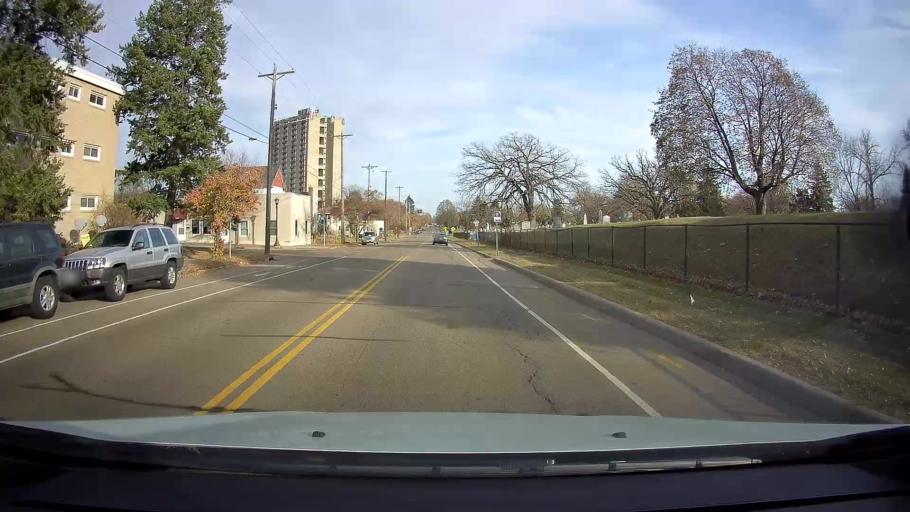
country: US
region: Minnesota
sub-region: Ramsey County
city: Falcon Heights
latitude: 44.9702
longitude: -93.1339
